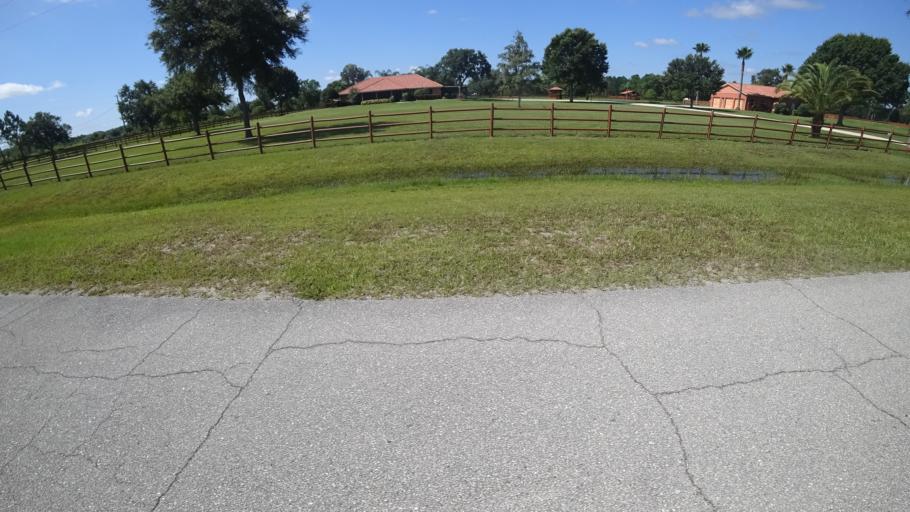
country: US
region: Florida
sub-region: Sarasota County
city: The Meadows
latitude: 27.4184
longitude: -82.3128
